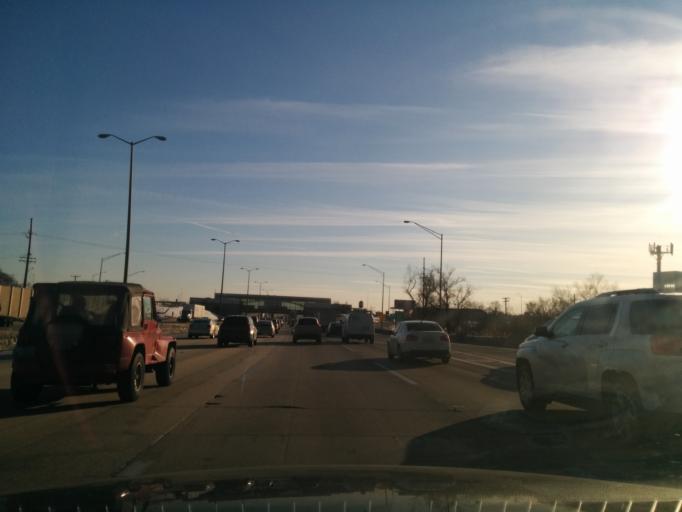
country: US
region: Illinois
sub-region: Cook County
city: Schiller Park
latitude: 41.9541
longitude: -87.8817
